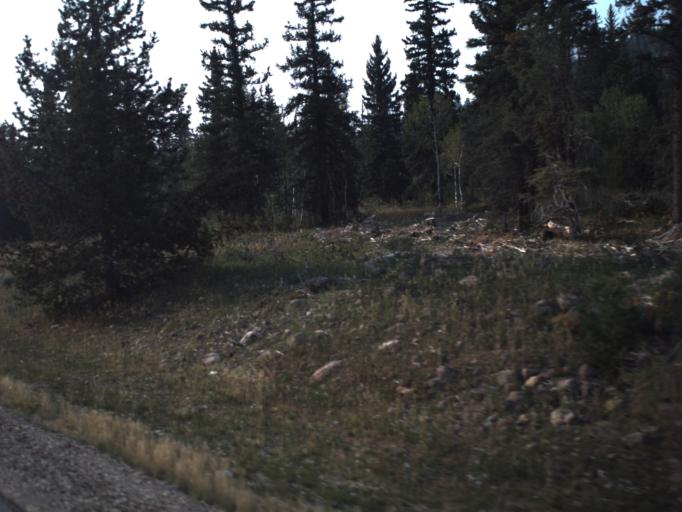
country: US
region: Utah
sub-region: Summit County
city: Francis
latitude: 40.5873
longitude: -111.0621
